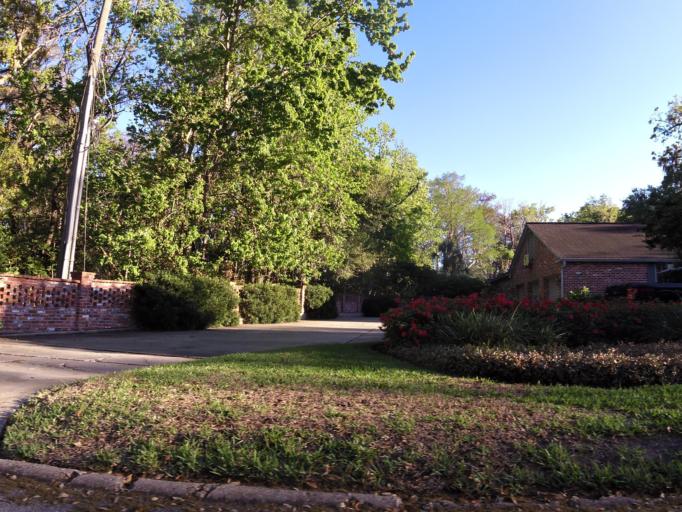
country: US
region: Florida
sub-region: Duval County
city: Jacksonville
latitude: 30.2468
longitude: -81.6361
